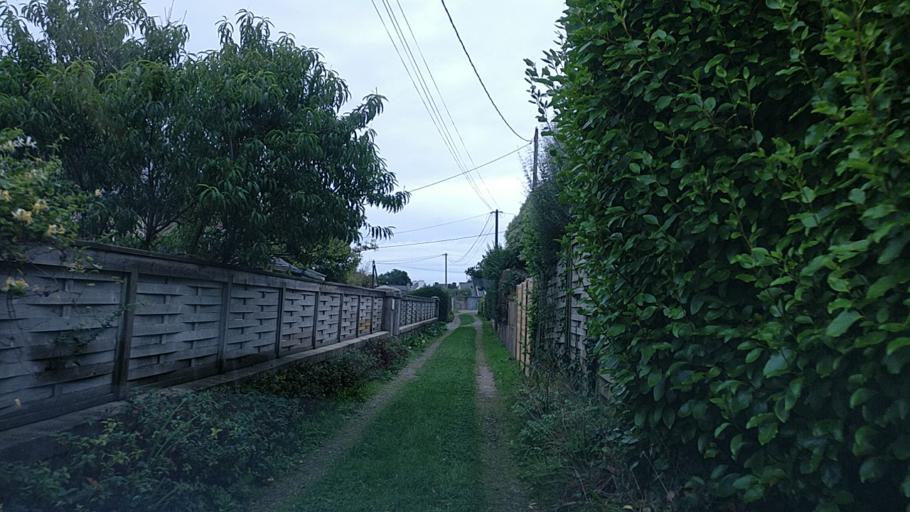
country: FR
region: Brittany
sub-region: Departement du Finistere
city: Saint-Pabu
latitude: 48.5713
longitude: -4.6078
